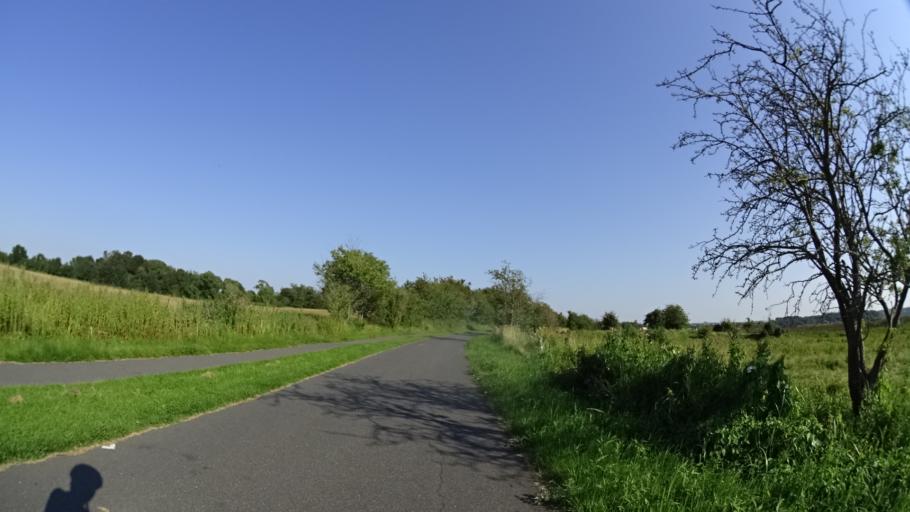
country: DK
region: Central Jutland
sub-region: Arhus Kommune
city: Stavtrup
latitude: 56.1446
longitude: 10.1359
